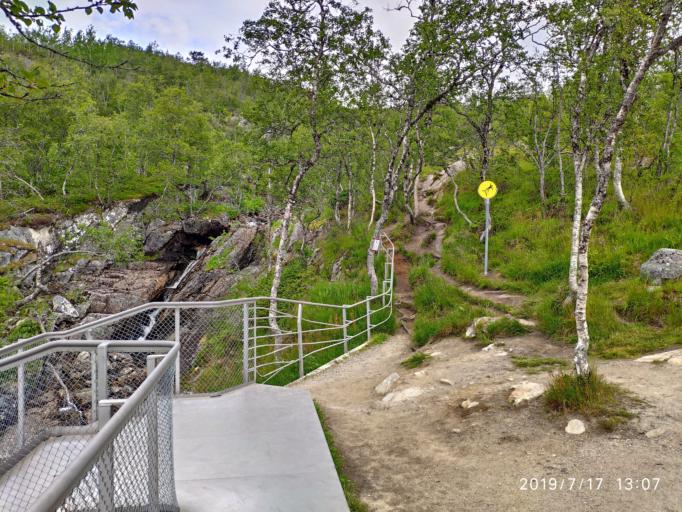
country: NO
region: Hordaland
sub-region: Eidfjord
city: Eidfjord
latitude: 60.4286
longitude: 7.2519
